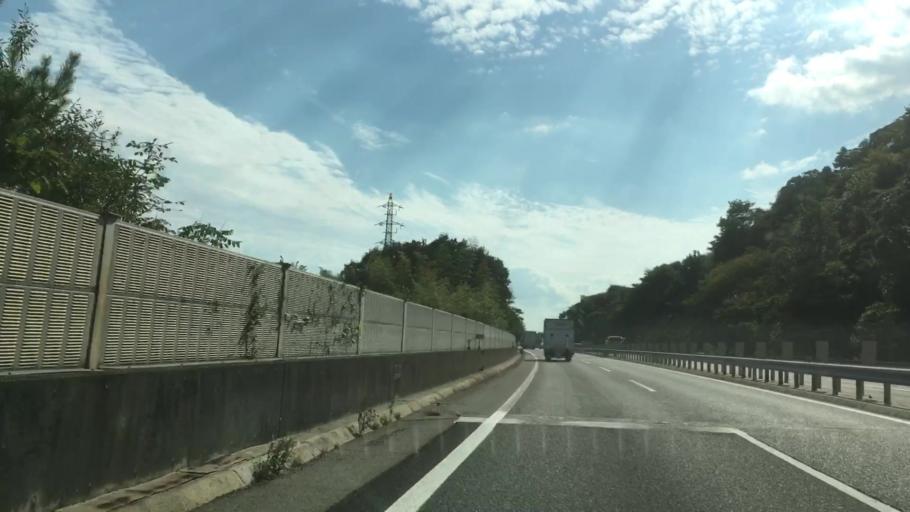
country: JP
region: Hiroshima
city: Ono-hara
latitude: 34.2831
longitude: 132.2605
